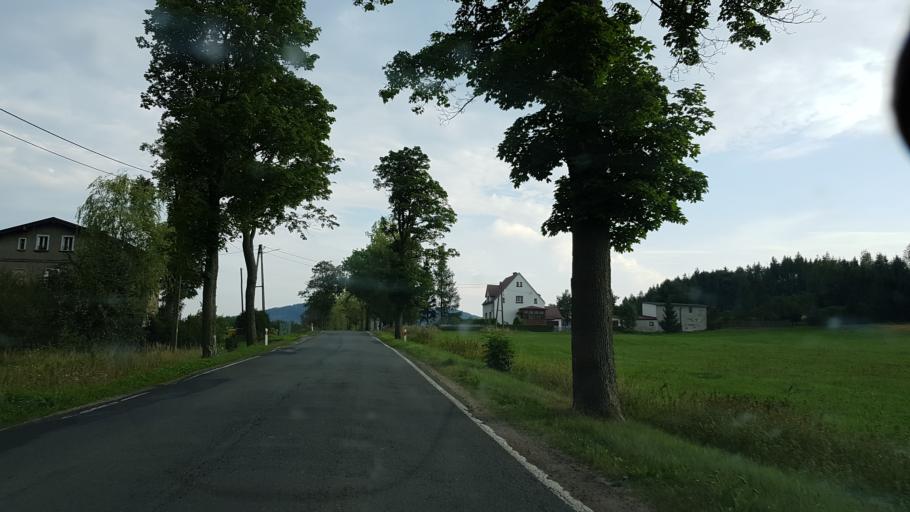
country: PL
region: Lower Silesian Voivodeship
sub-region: Powiat kamiennogorski
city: Marciszow
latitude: 50.8637
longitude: 16.0006
